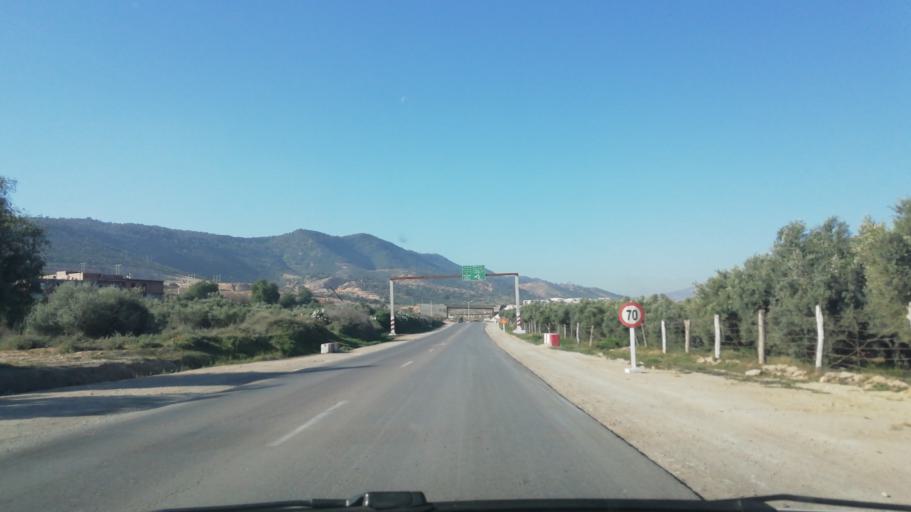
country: DZ
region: Mascara
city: Sig
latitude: 35.5320
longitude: -0.1461
